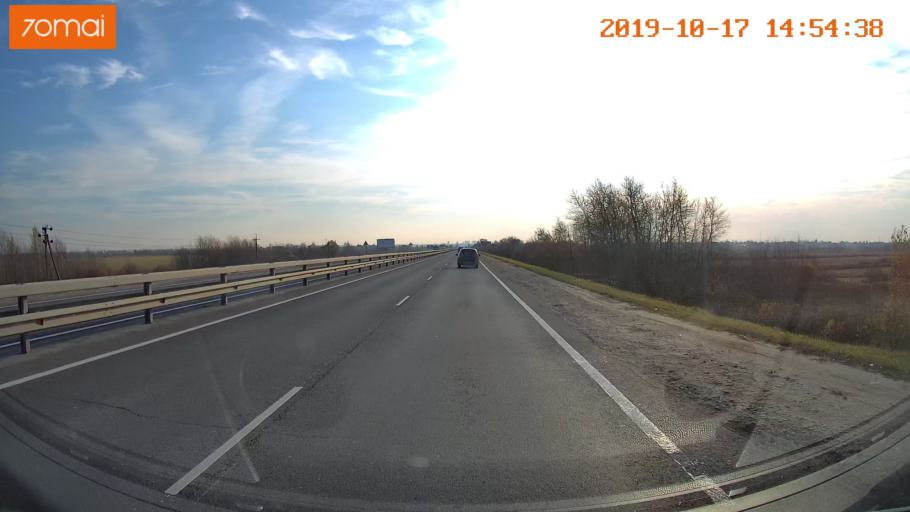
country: RU
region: Rjazan
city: Polyany
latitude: 54.6785
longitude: 39.8304
